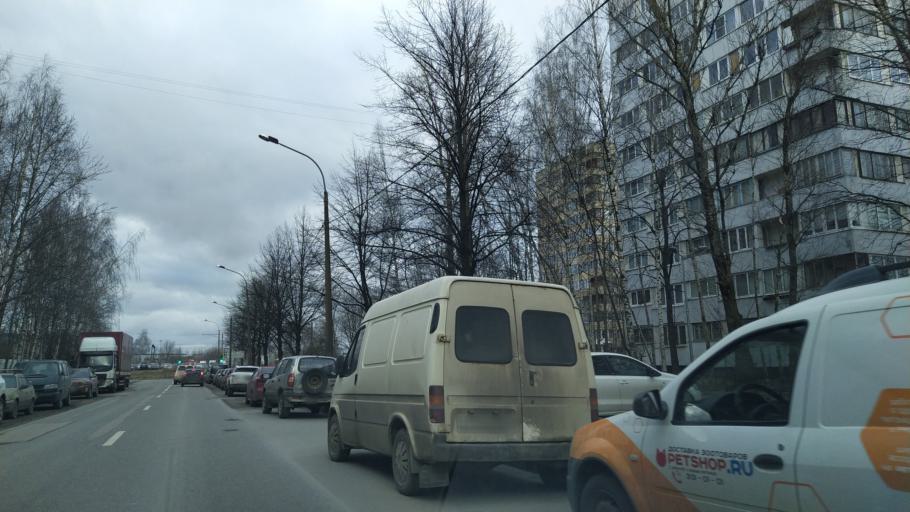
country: RU
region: Leningrad
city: Bugry
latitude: 60.0521
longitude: 30.3712
